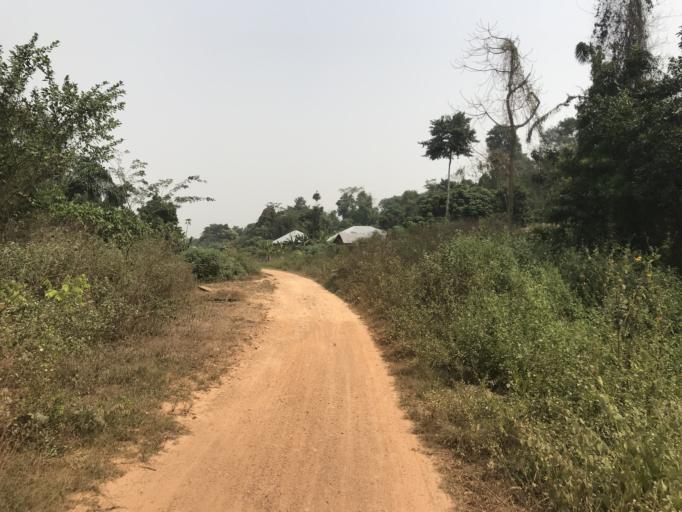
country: NG
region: Osun
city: Ifetedo
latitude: 7.0465
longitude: 4.4680
